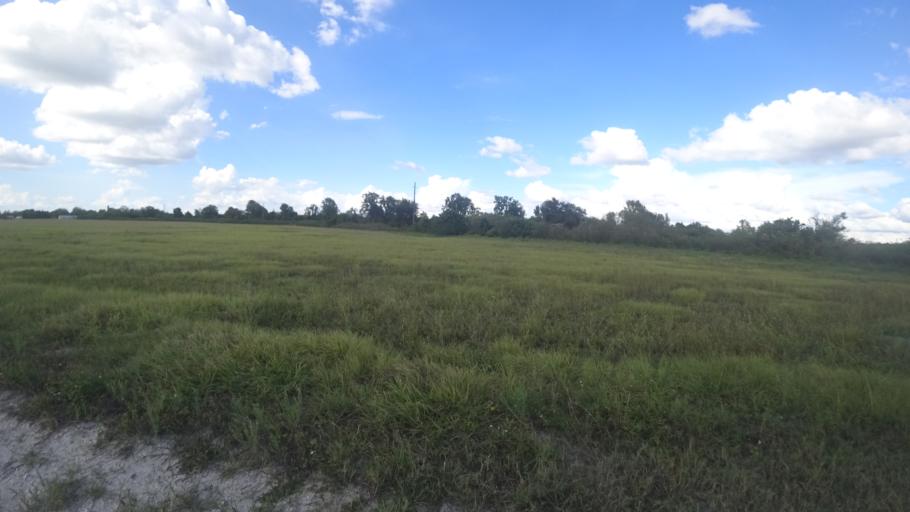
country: US
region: Florida
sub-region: DeSoto County
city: Arcadia
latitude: 27.2993
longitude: -82.1208
